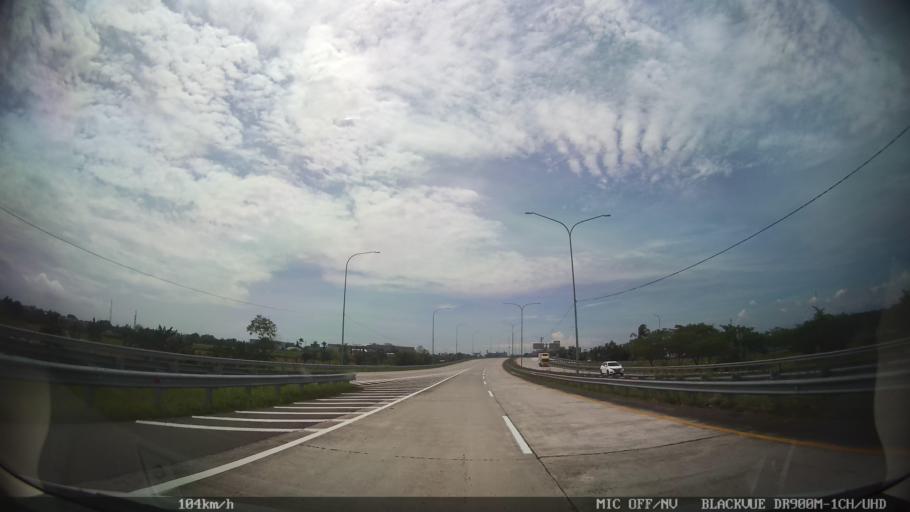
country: ID
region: North Sumatra
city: Percut
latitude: 3.5610
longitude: 98.8509
